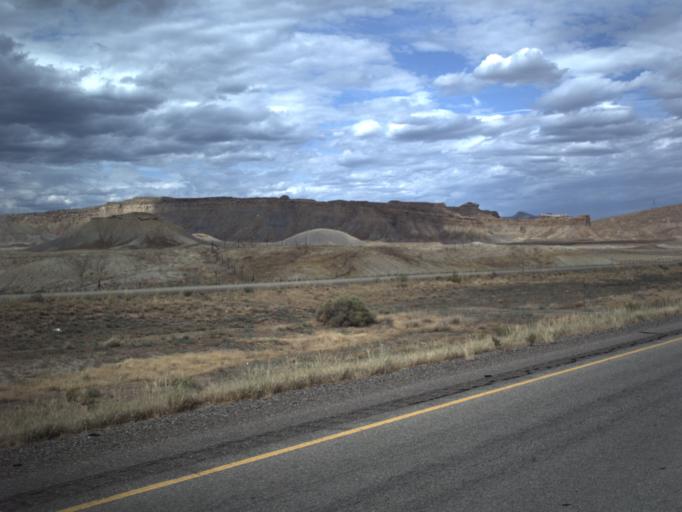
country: US
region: Utah
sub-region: Grand County
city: Moab
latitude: 38.9258
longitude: -109.9036
